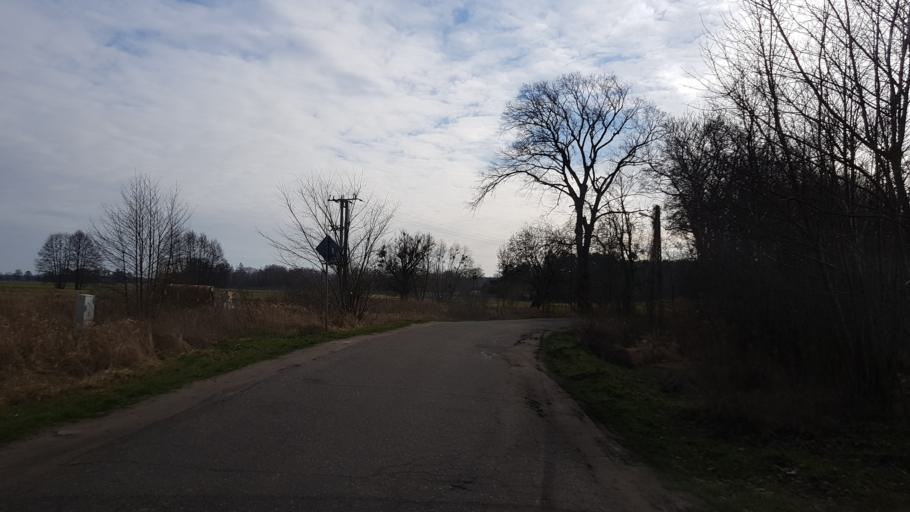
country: PL
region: West Pomeranian Voivodeship
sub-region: Powiat policki
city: Dobra
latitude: 53.5171
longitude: 14.3501
